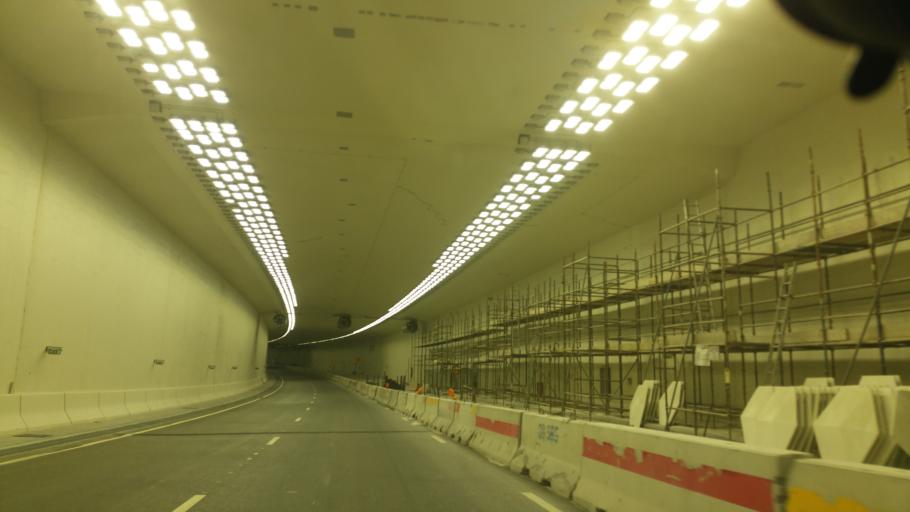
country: QA
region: Baladiyat Umm Salal
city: Umm Salal Muhammad
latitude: 25.4193
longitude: 51.5059
